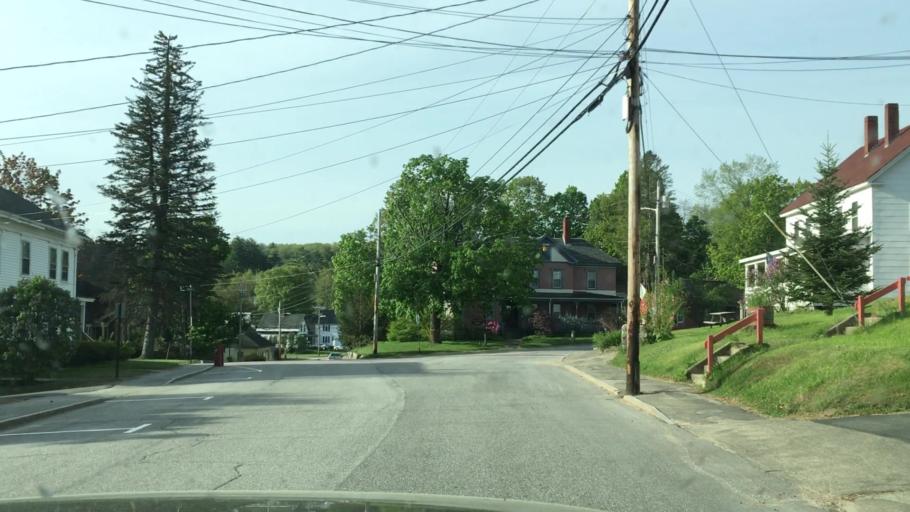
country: US
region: New Hampshire
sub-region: Belknap County
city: Meredith
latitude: 43.6538
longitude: -71.5002
